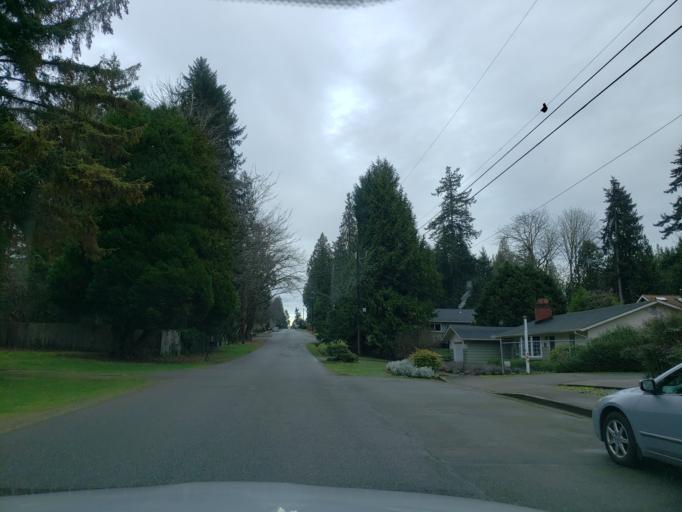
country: US
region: Washington
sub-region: Snohomish County
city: Edmonds
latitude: 47.8251
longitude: -122.3507
